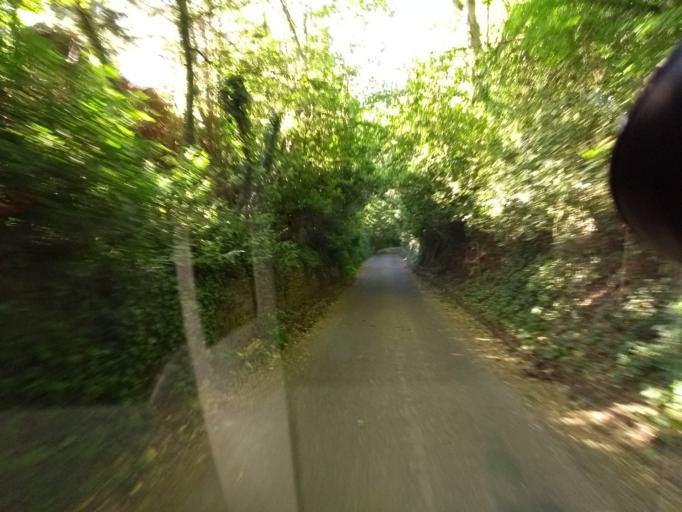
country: GB
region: England
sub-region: Somerset
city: Creech Saint Michael
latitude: 51.0486
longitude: -3.0534
